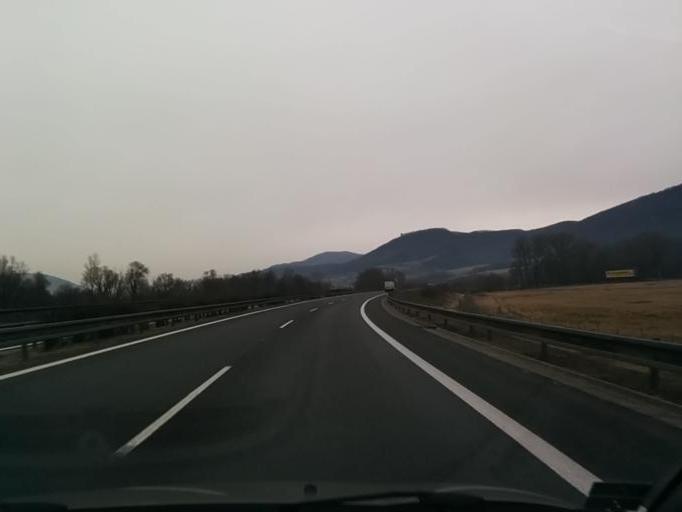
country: SK
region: Banskobystricky
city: Nova Bana
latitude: 48.3711
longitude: 18.5941
